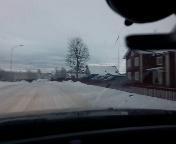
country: SE
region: Gaevleborg
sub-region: Bollnas Kommun
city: Bollnas
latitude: 61.3558
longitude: 16.3841
